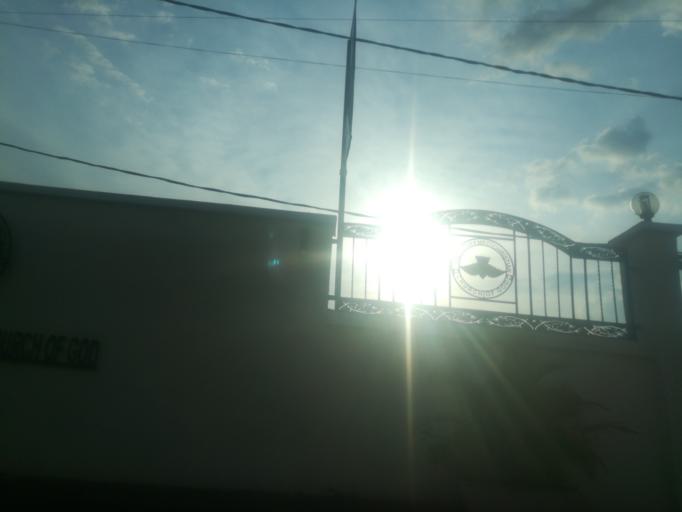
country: NG
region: Oyo
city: Ibadan
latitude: 7.3853
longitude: 3.8808
